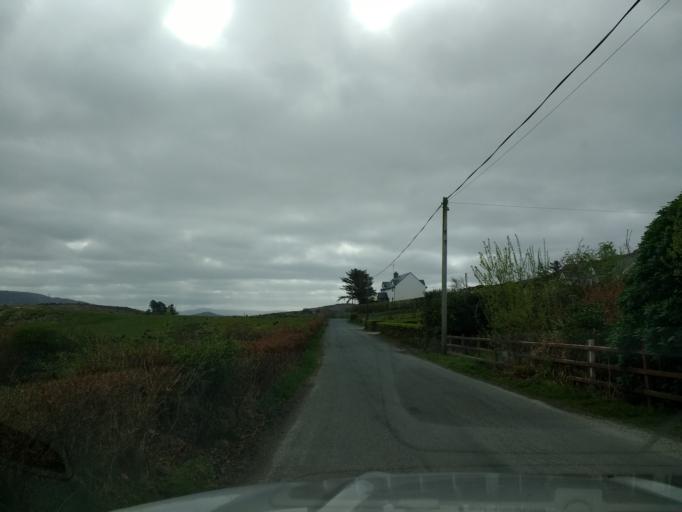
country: IE
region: Ulster
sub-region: County Donegal
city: Buncrana
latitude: 55.2444
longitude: -7.6241
